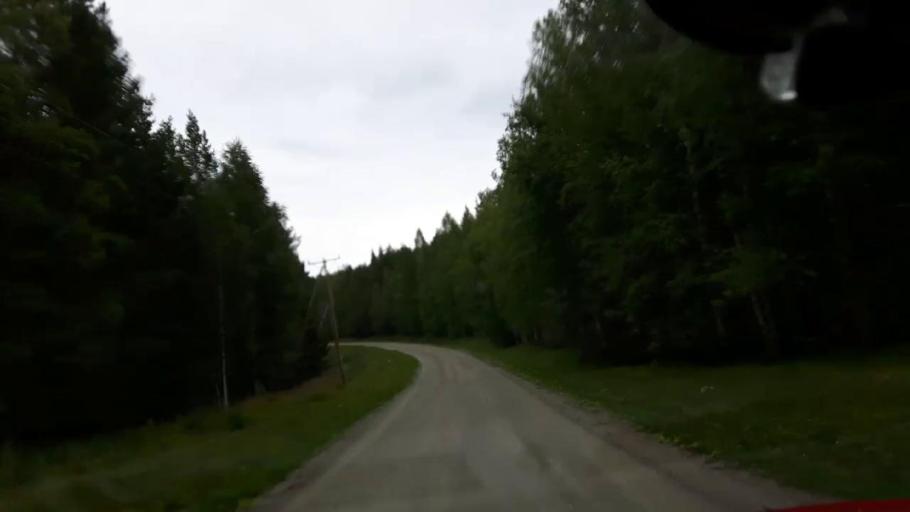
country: SE
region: Vaesternorrland
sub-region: Ange Kommun
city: Fransta
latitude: 62.7768
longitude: 16.1605
